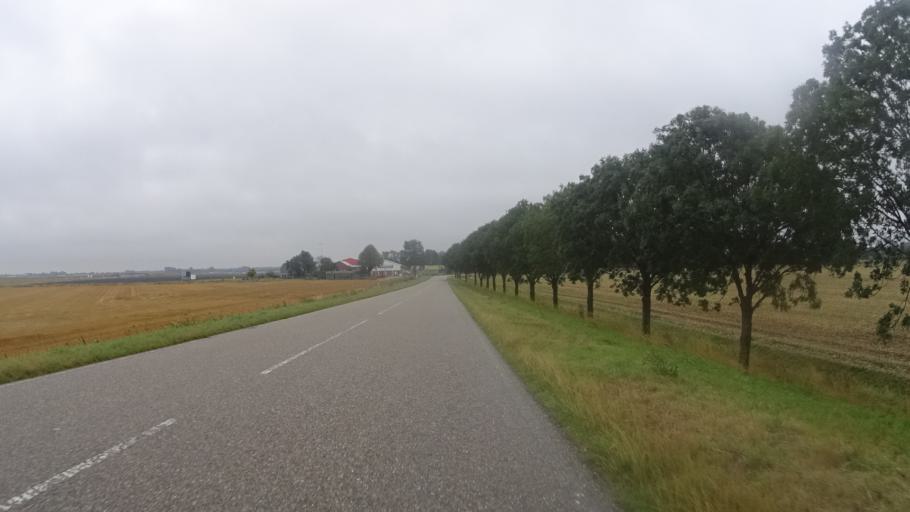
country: NL
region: Groningen
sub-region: Gemeente  Oldambt
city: Winschoten
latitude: 53.1861
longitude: 6.9472
